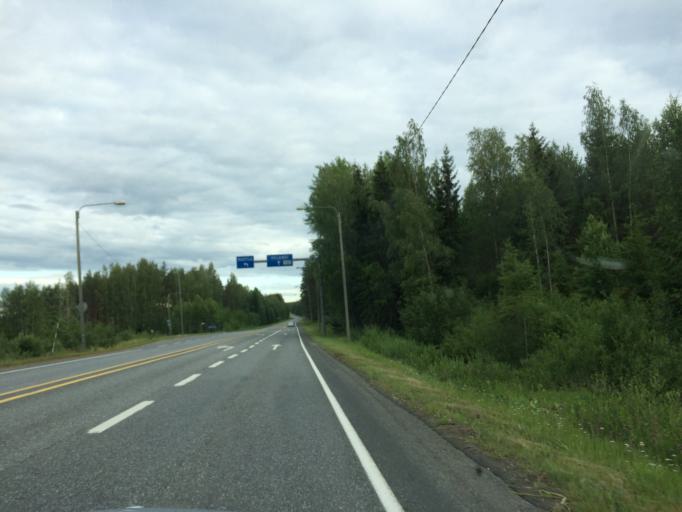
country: FI
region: Haeme
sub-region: Haemeenlinna
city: Haemeenlinna
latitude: 60.9423
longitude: 24.5183
